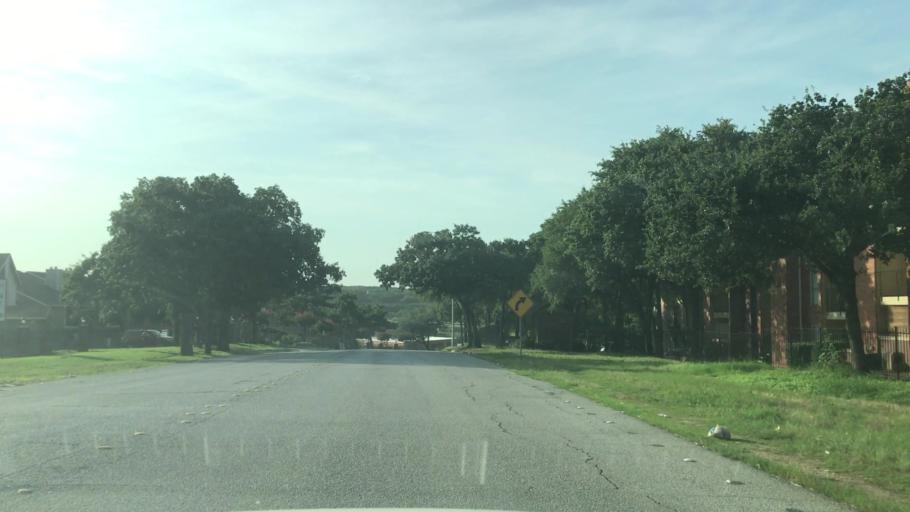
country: US
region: Texas
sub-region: Tarrant County
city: Pantego
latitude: 32.7596
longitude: -97.1578
